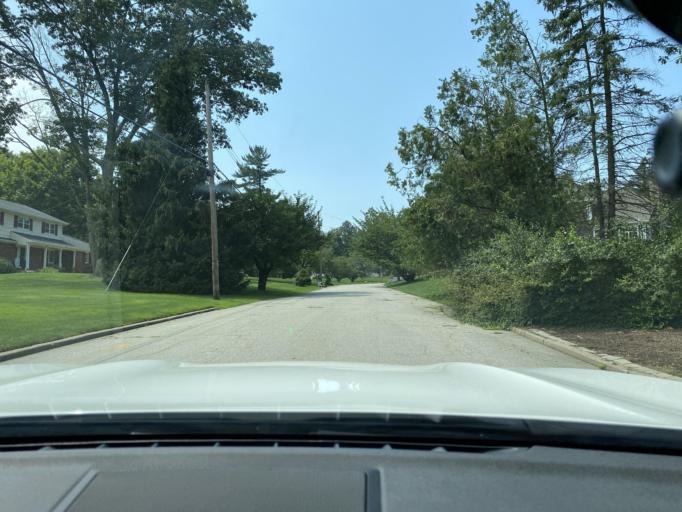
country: US
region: New York
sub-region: Rockland County
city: Airmont
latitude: 41.0873
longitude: -74.1075
